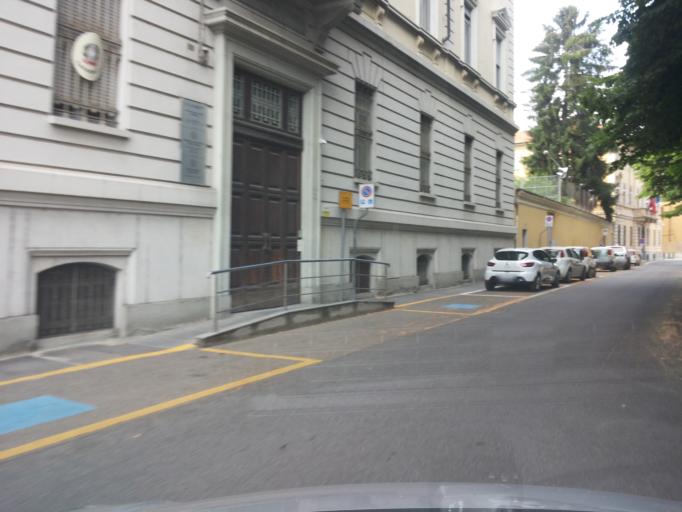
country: IT
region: Piedmont
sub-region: Provincia di Vercelli
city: Vercelli
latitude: 45.3222
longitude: 8.4248
